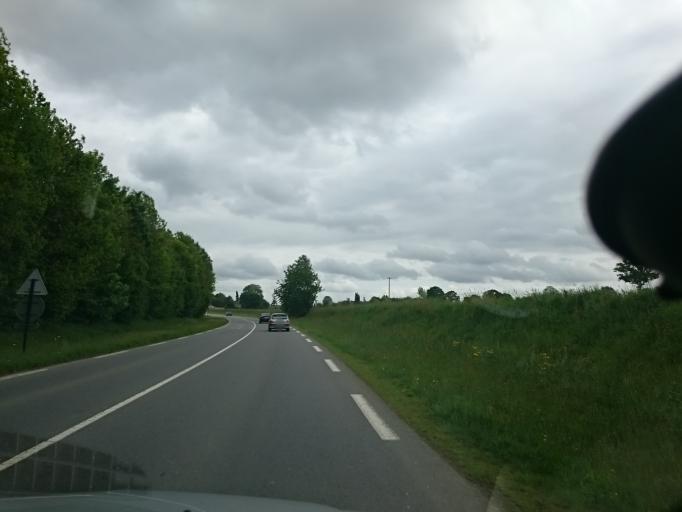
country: FR
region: Brittany
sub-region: Departement d'Ille-et-Vilaine
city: Antrain
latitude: 48.4463
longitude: -1.4732
